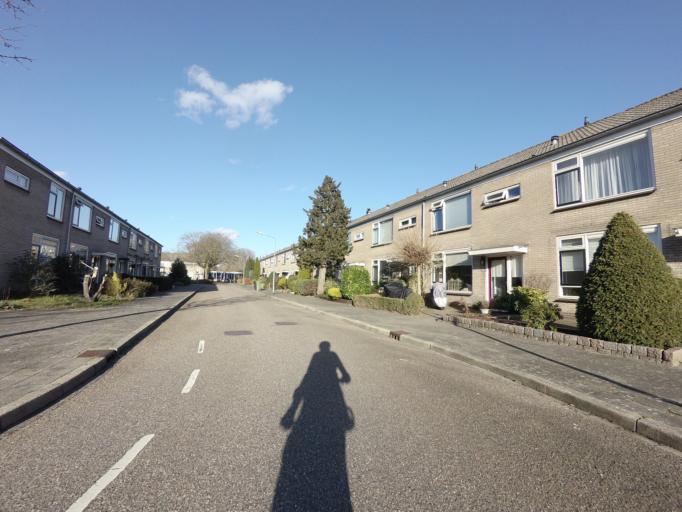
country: NL
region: North Holland
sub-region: Gemeente Wijdemeren
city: Nieuw-Loosdrecht
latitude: 52.2173
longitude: 5.1344
